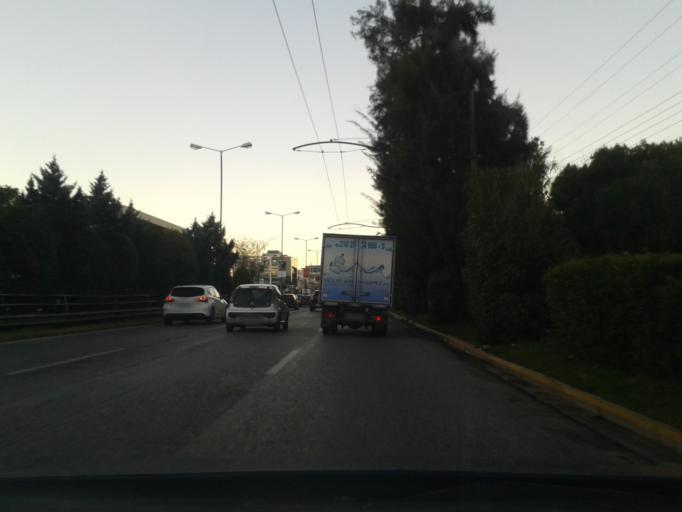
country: GR
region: Attica
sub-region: Nomarchia Athinas
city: Filothei
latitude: 38.0186
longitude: 23.7877
